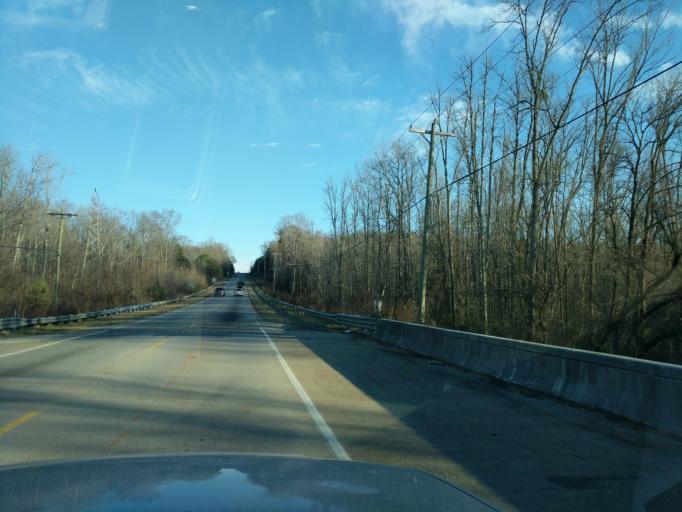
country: US
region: South Carolina
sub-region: Anderson County
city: Williamston
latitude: 34.6379
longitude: -82.4250
